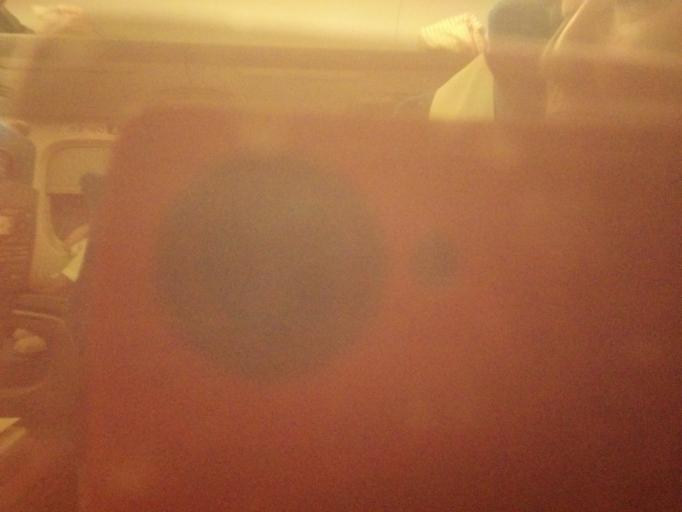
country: JP
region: Shizuoka
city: Mishima
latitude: 35.1085
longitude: 138.9787
